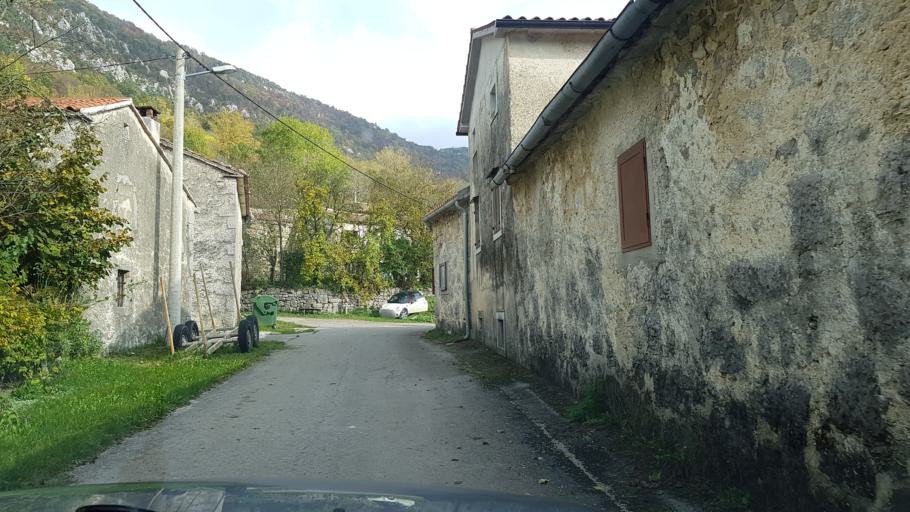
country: HR
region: Istarska
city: Buzet
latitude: 45.4240
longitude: 14.0743
